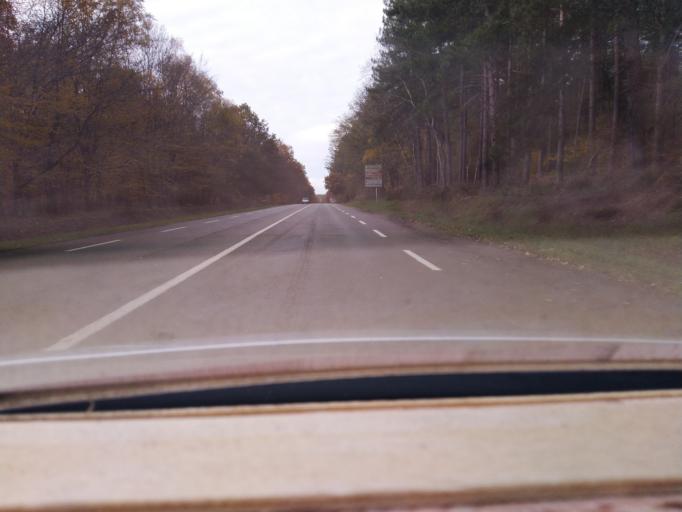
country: FR
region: Haute-Normandie
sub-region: Departement de la Seine-Maritime
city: Canteleu
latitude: 49.4451
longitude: 1.0093
